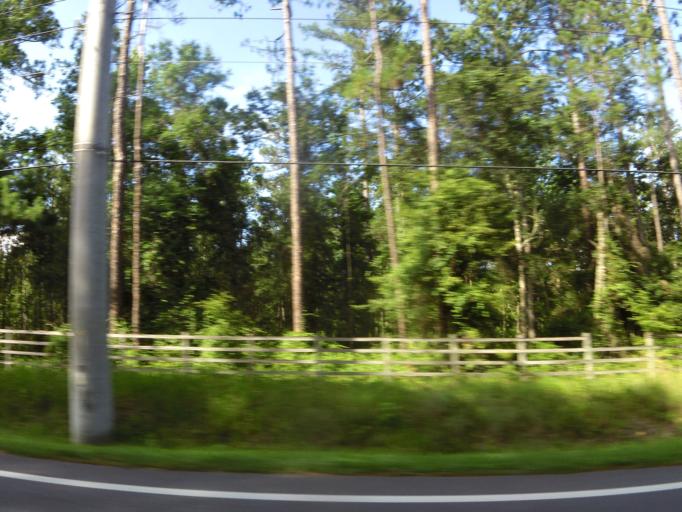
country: US
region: Florida
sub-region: Clay County
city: Green Cove Springs
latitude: 30.0112
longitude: -81.5566
